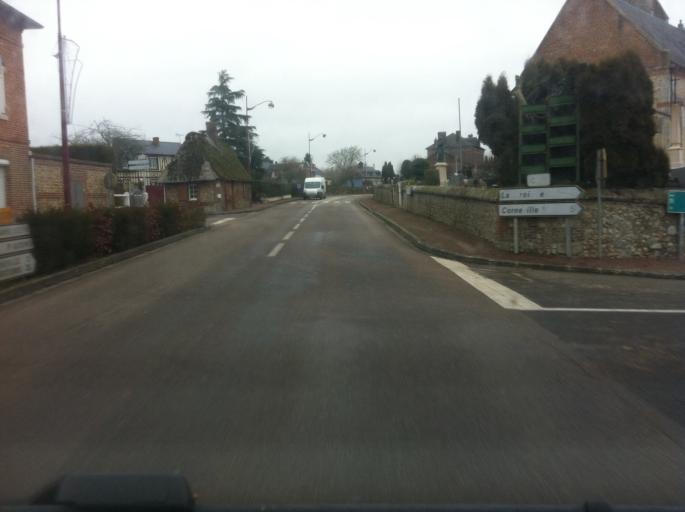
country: FR
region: Haute-Normandie
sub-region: Departement de l'Eure
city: Manneville-sur-Risle
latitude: 49.3812
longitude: 0.5716
